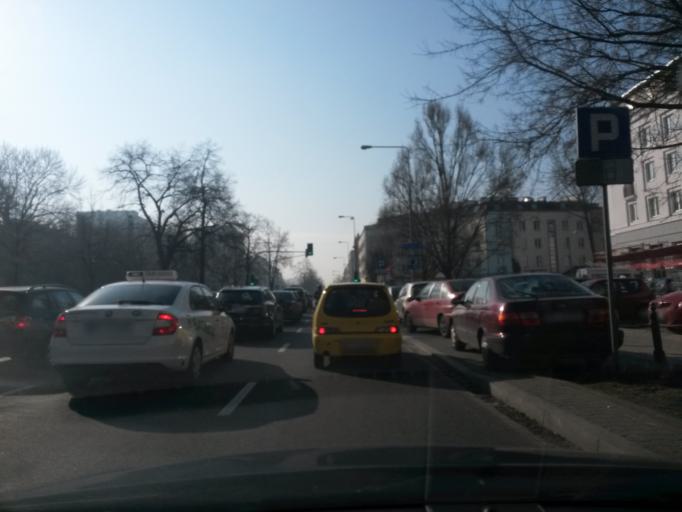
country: PL
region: Masovian Voivodeship
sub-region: Warszawa
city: Mokotow
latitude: 52.1953
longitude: 21.0240
